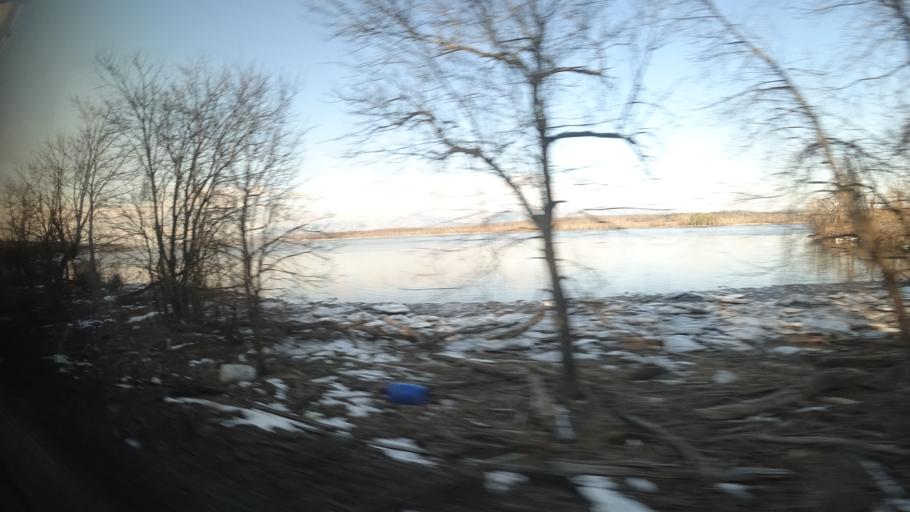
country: US
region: New York
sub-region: Greene County
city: Catskill
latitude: 42.1904
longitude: -73.8512
